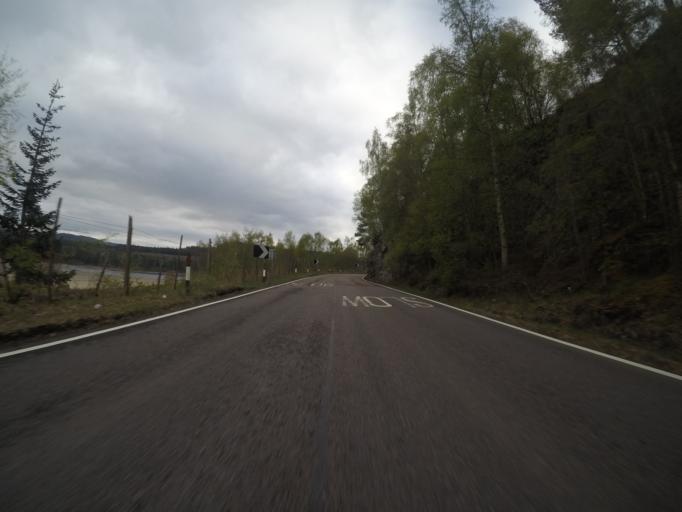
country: GB
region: Scotland
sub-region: Highland
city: Kingussie
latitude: 56.9737
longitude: -4.4208
